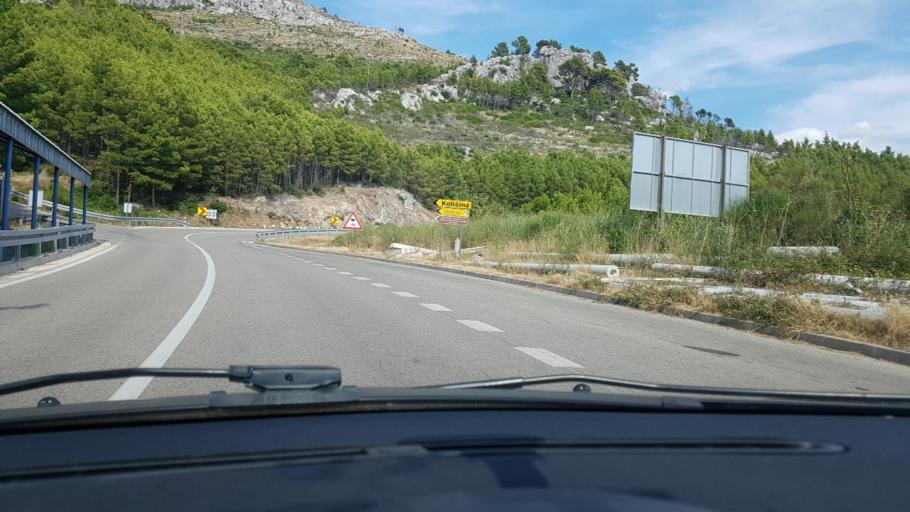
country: HR
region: Splitsko-Dalmatinska
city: Tucepi
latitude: 43.2825
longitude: 17.0414
